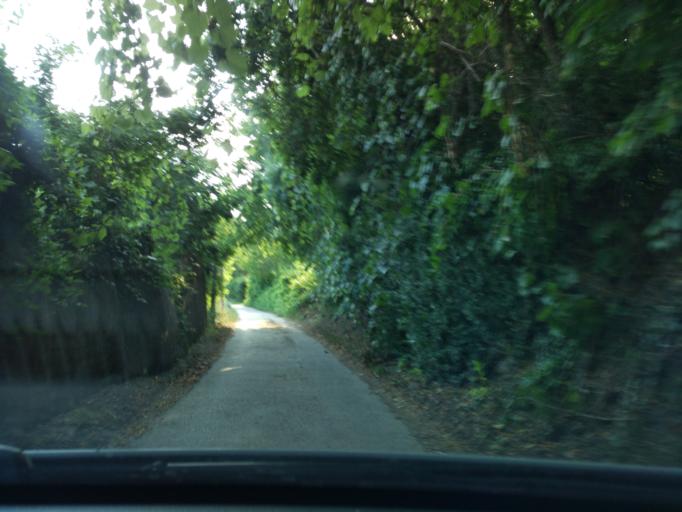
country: HU
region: Veszprem
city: Badacsonytomaj
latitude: 46.8103
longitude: 17.5425
